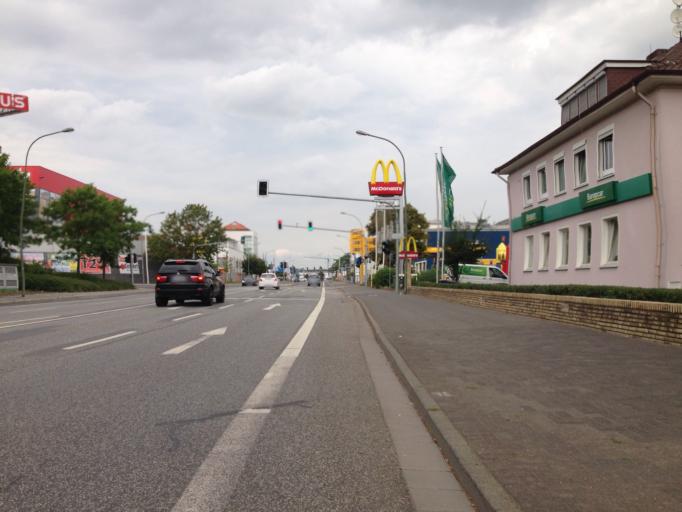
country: DE
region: Hesse
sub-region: Regierungsbezirk Giessen
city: Giessen
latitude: 50.5721
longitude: 8.6896
